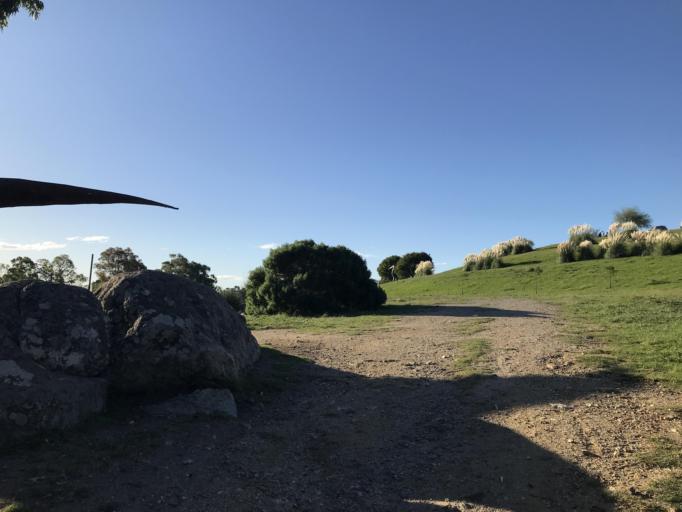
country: AR
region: Buenos Aires
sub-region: Partido de Tandil
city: Tandil
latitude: -37.3375
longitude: -59.1129
